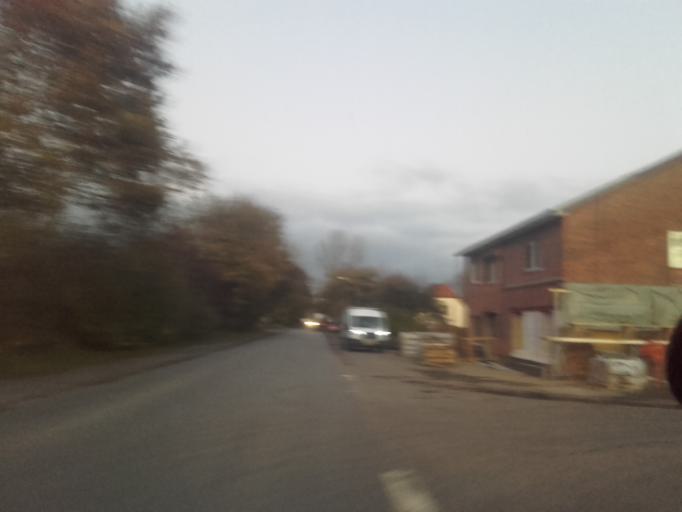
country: DE
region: Schleswig-Holstein
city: Dorpstedt
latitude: 54.4405
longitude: 9.3609
